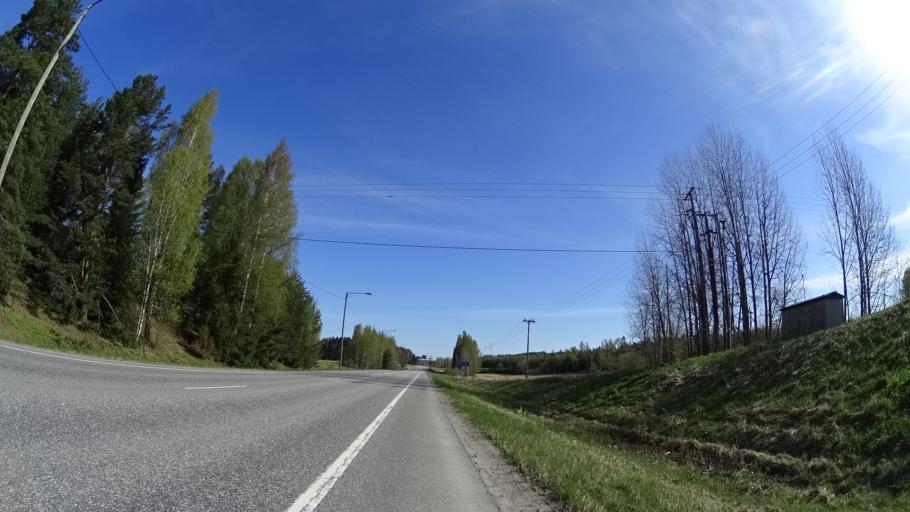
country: FI
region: Uusimaa
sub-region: Helsinki
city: Nurmijaervi
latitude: 60.3924
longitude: 24.8107
